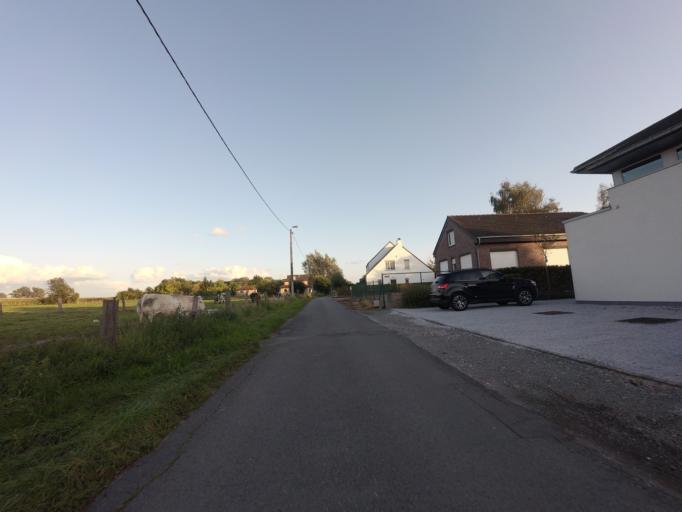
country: BE
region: Flanders
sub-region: Provincie Vlaams-Brabant
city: Londerzeel
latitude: 50.9945
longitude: 4.3256
